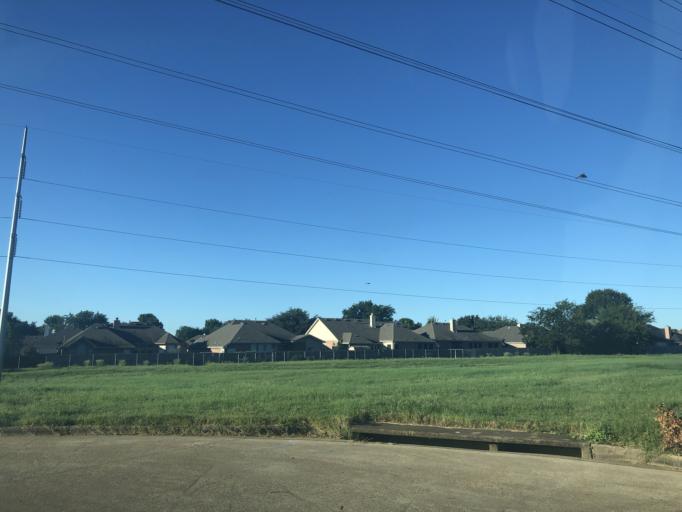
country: US
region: Texas
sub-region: Dallas County
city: Grand Prairie
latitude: 32.6638
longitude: -96.9985
